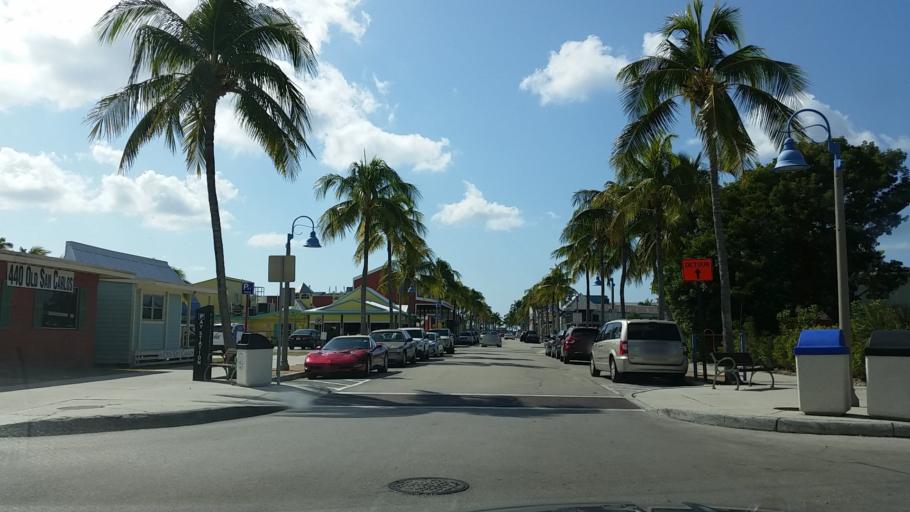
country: US
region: Florida
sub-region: Lee County
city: Fort Myers Beach
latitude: 26.4559
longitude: -81.9548
